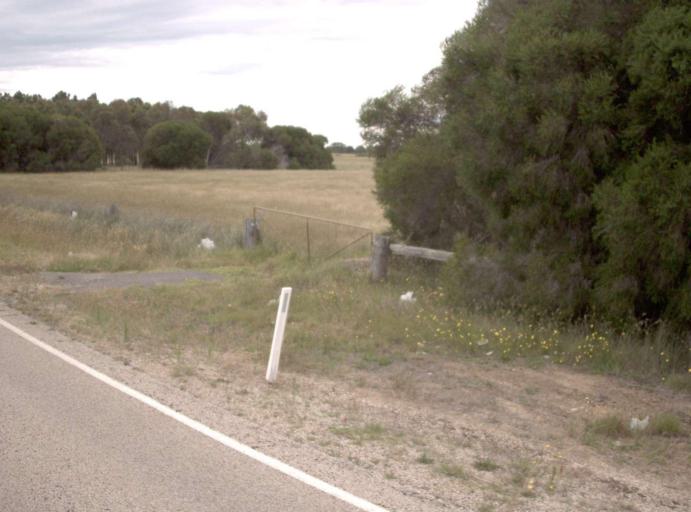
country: AU
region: Victoria
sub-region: East Gippsland
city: Bairnsdale
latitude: -37.8851
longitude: 147.5579
